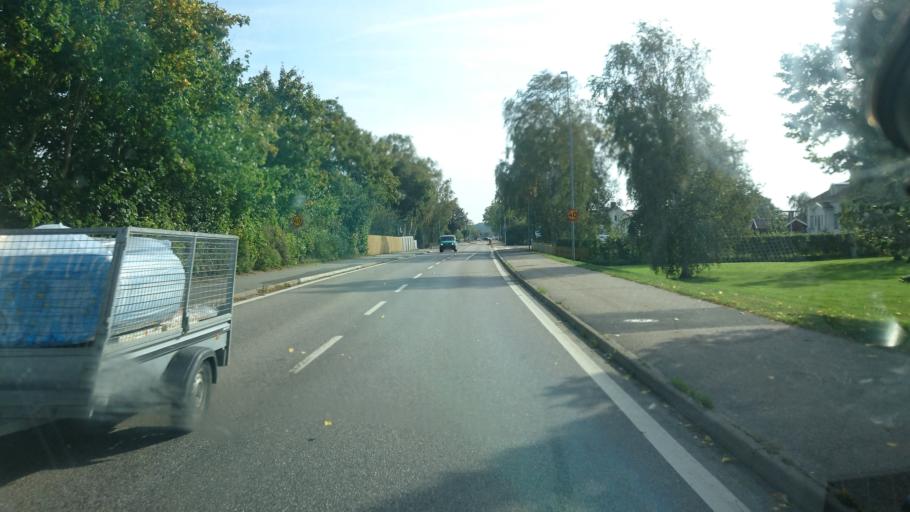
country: SE
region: Vaestra Goetaland
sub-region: Alingsas Kommun
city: Sollebrunn
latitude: 58.1221
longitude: 12.5255
